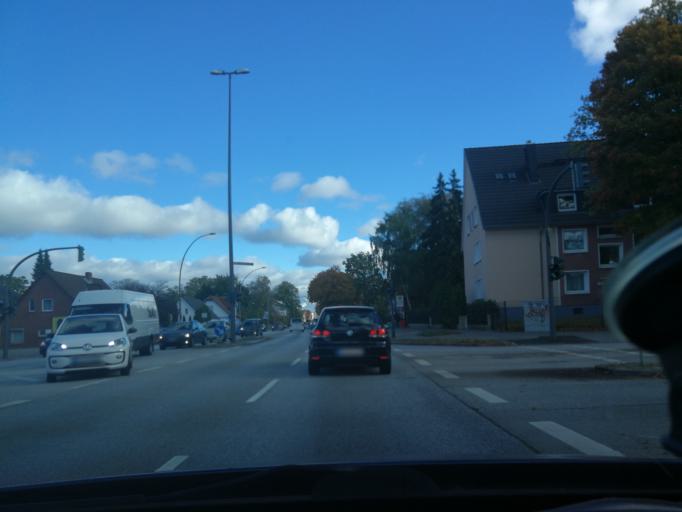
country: DE
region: Lower Saxony
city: Neu Wulmstorf
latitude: 53.4722
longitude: 9.8398
